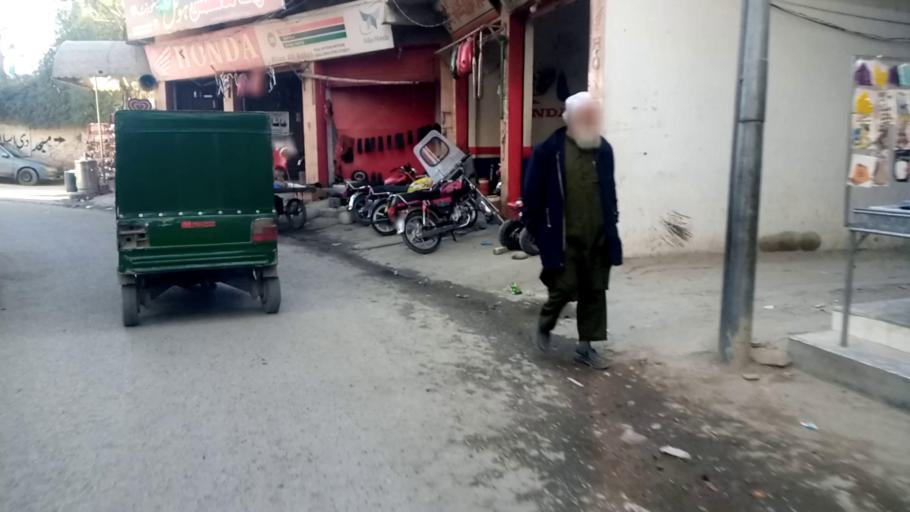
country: PK
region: Khyber Pakhtunkhwa
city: Mingora
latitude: 34.7841
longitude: 72.3604
